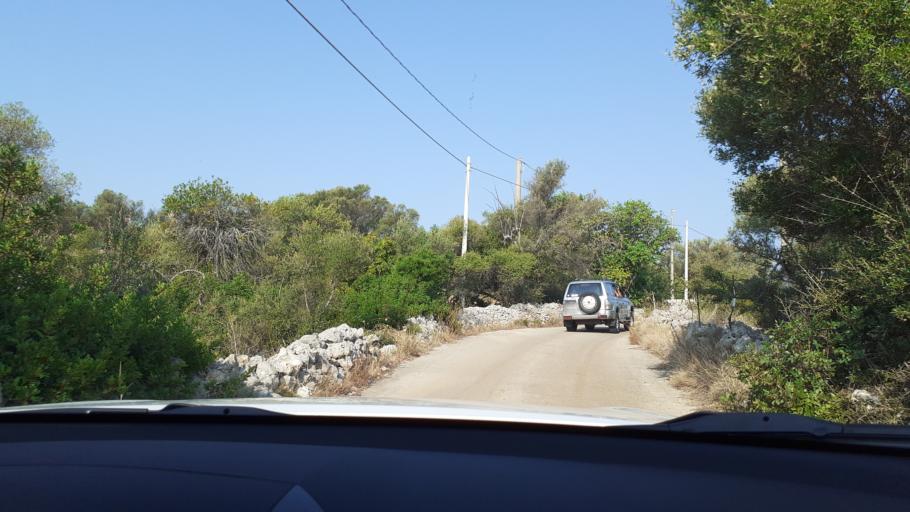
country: IT
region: Sicily
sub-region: Provincia di Siracusa
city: Cassibile
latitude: 36.9767
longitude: 15.1555
